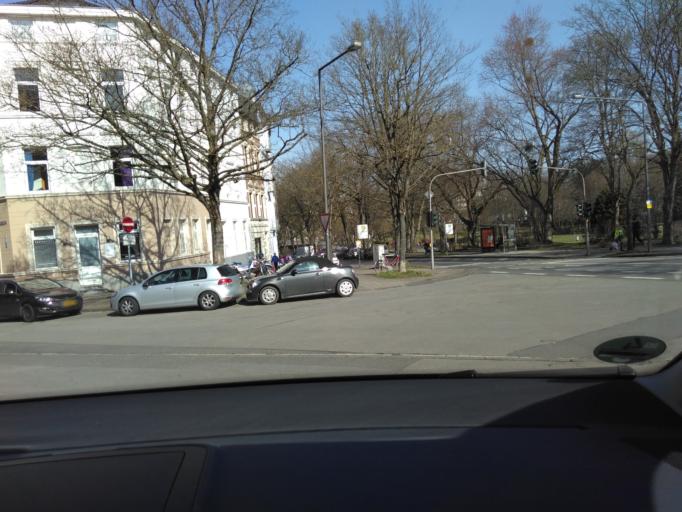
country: DE
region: North Rhine-Westphalia
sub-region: Regierungsbezirk Koln
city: Aachen
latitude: 50.7587
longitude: 6.0944
